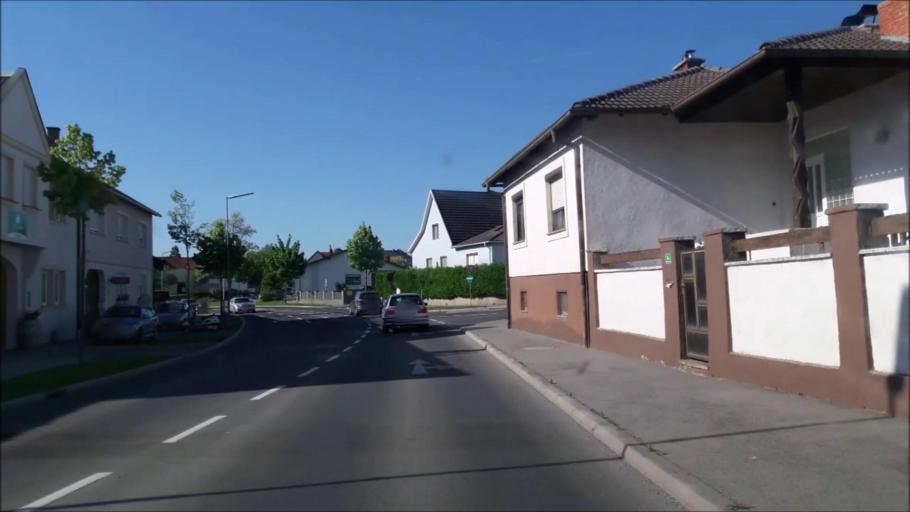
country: AT
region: Burgenland
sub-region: Eisenstadt-Umgebung
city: Sankt Margarethen im Burgenland
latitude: 47.8081
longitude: 16.6059
